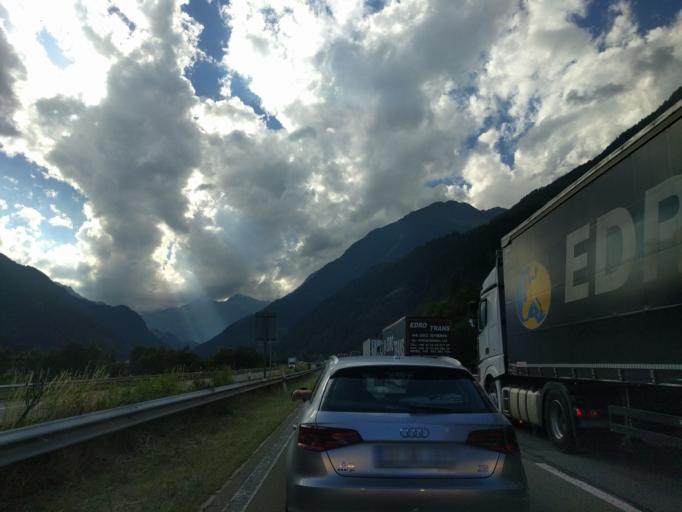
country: CH
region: Ticino
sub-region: Leventina District
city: Airolo
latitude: 46.5107
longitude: 8.7067
